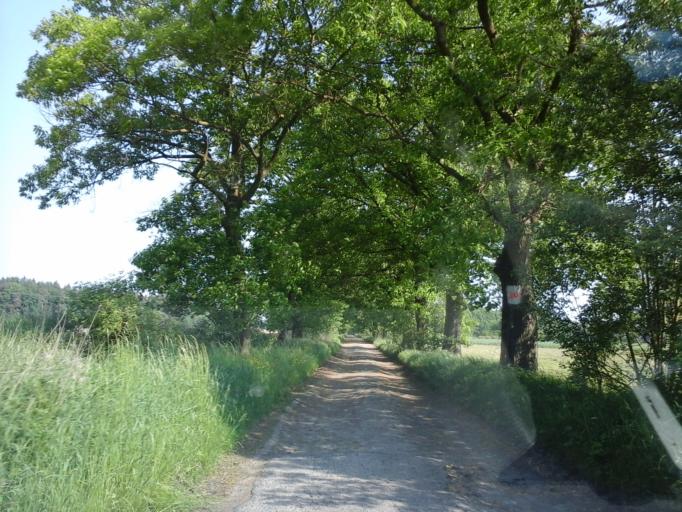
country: PL
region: West Pomeranian Voivodeship
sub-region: Powiat choszczenski
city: Recz
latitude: 53.2918
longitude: 15.5379
